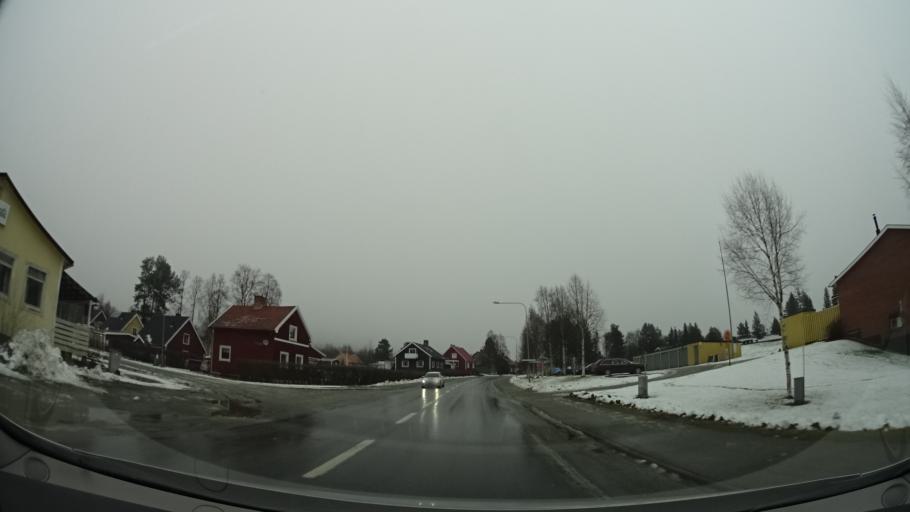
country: SE
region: Vaesterbotten
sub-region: Dorotea Kommun
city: Dorotea
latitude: 64.2591
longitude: 16.3963
